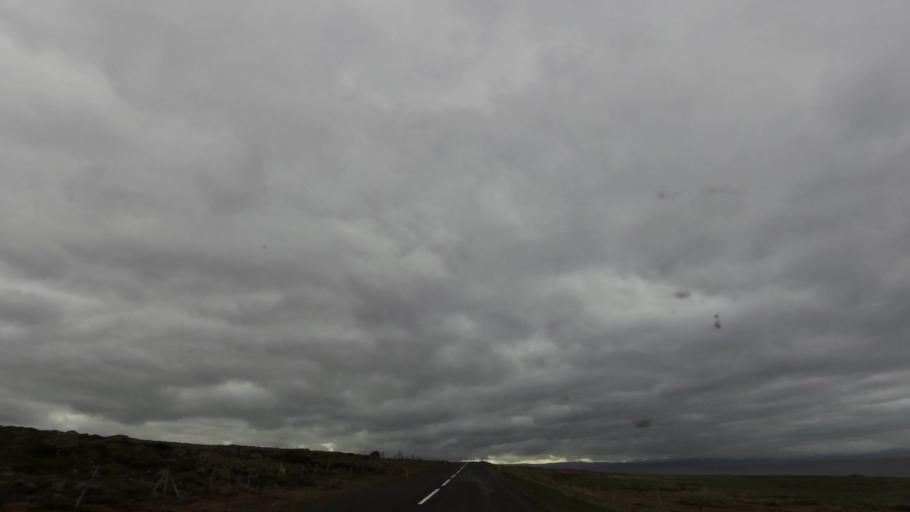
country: IS
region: West
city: Borgarnes
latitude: 65.1239
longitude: -21.7427
